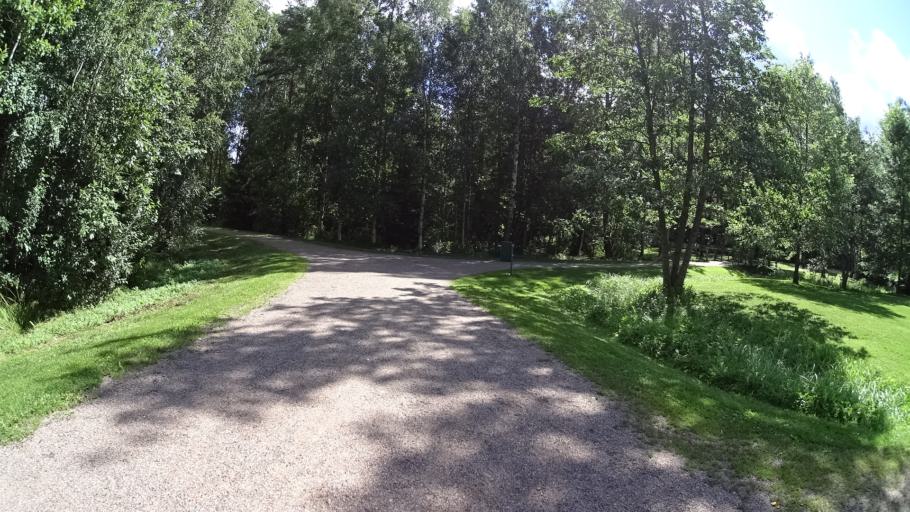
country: FI
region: Uusimaa
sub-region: Helsinki
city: Teekkarikylae
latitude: 60.2854
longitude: 24.8569
